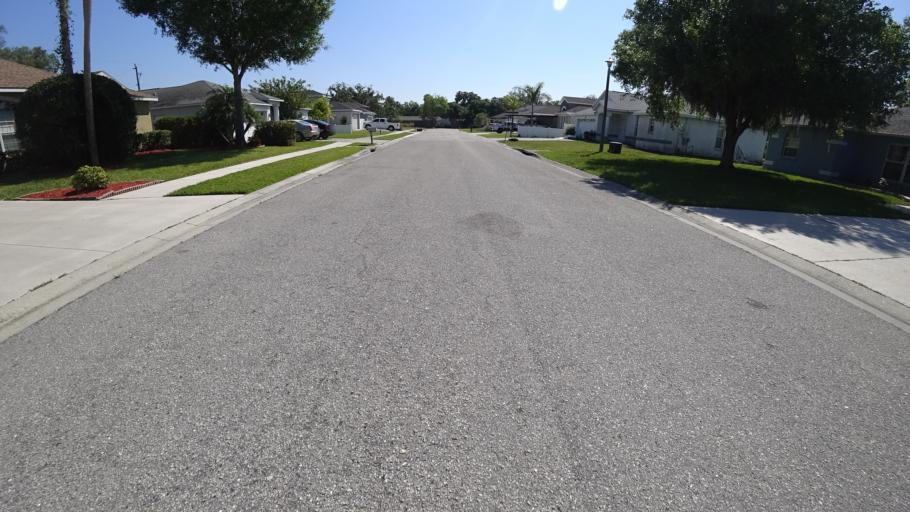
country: US
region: Florida
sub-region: Manatee County
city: Samoset
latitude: 27.4689
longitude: -82.5244
